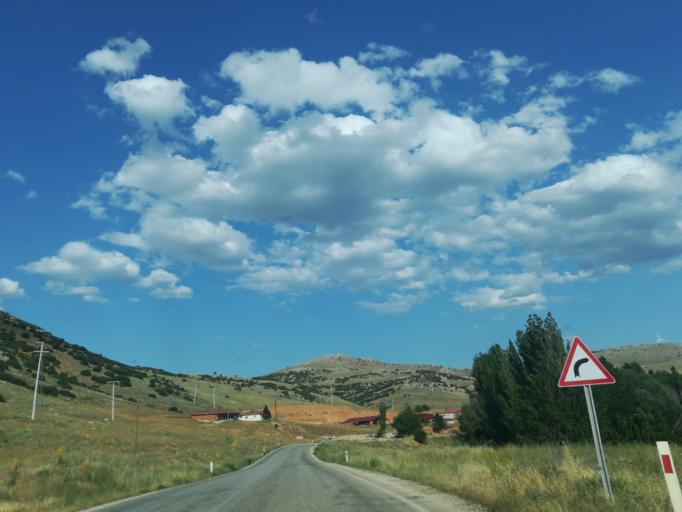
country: TR
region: Afyonkarahisar
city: Dinar
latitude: 38.0992
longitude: 30.1539
